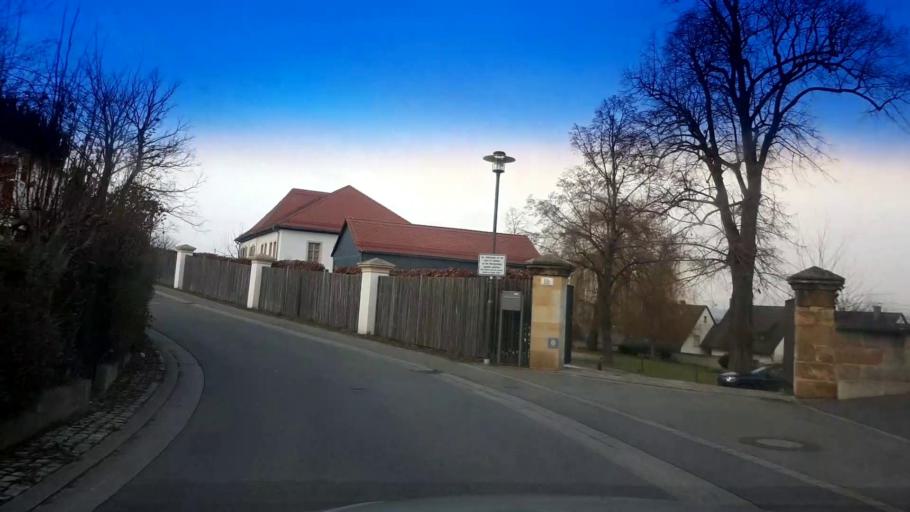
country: DE
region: Bavaria
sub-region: Upper Franconia
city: Hirschaid
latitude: 49.8053
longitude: 10.9852
